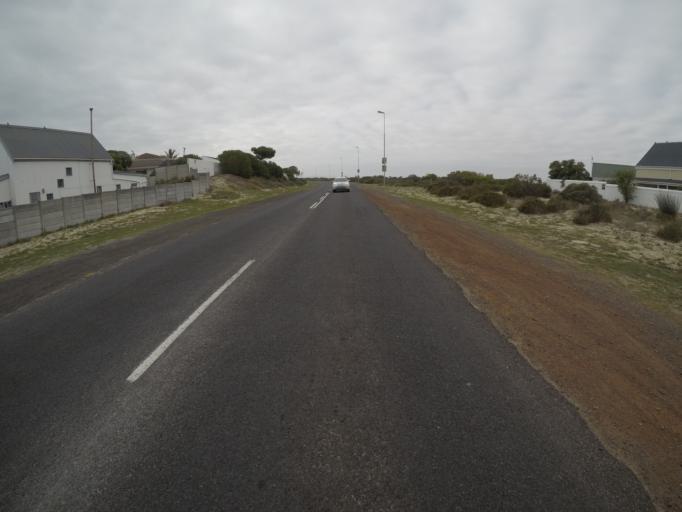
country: ZA
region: Western Cape
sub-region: City of Cape Town
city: Atlantis
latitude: -33.7107
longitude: 18.4466
